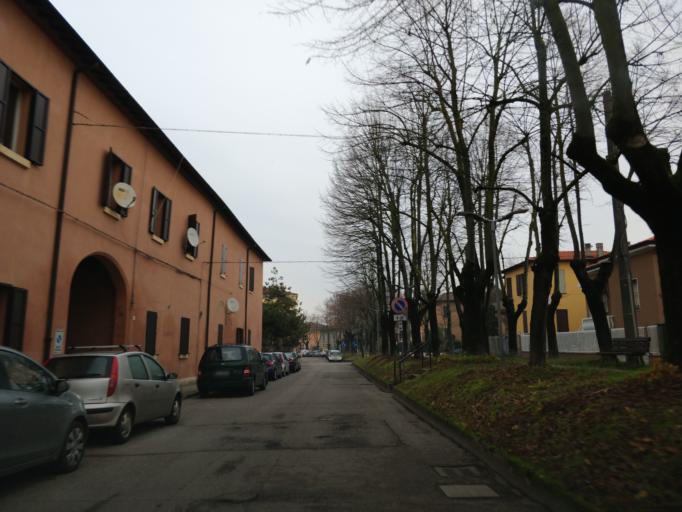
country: IT
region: Emilia-Romagna
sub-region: Provincia di Ferrara
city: Cento
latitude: 44.7256
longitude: 11.2924
